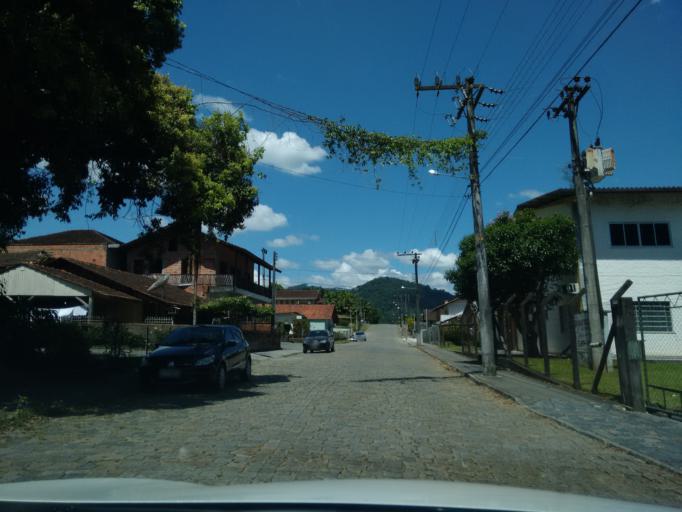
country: BR
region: Santa Catarina
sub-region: Pomerode
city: Pomerode
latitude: -26.7508
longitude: -49.1793
